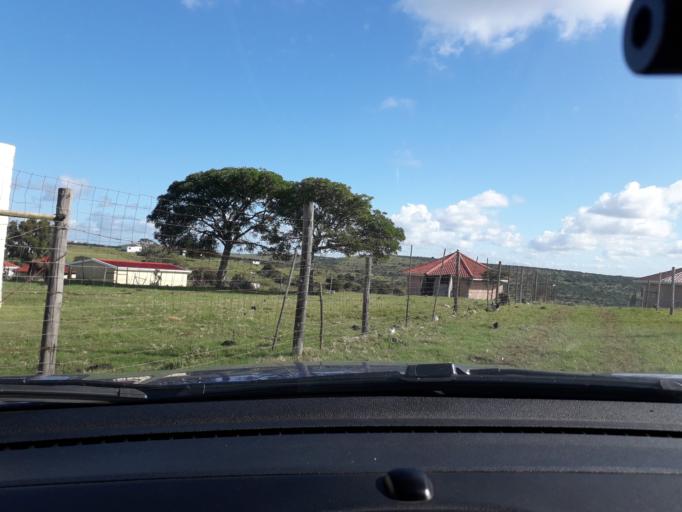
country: ZA
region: Eastern Cape
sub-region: Buffalo City Metropolitan Municipality
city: Bhisho
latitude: -33.1098
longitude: 27.4245
